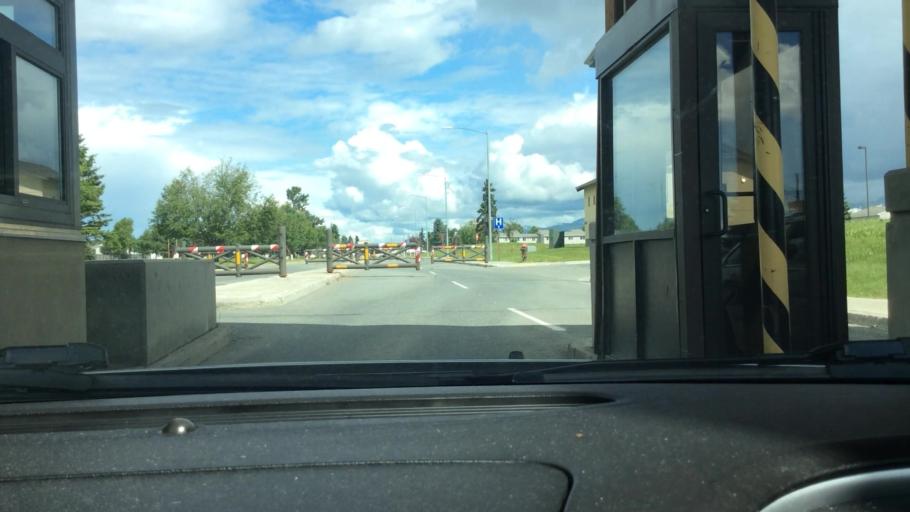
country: US
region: Alaska
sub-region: Anchorage Municipality
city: Anchorage
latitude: 61.2319
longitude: -149.8705
